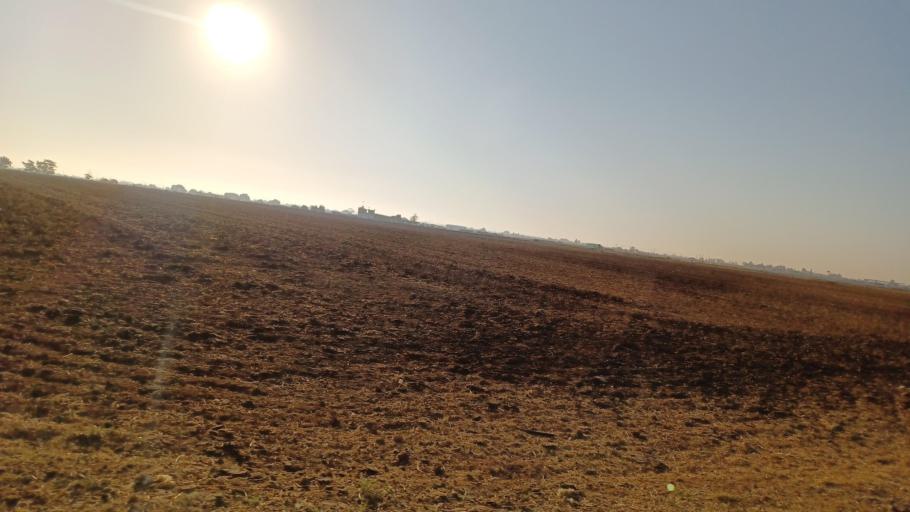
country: CY
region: Ammochostos
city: Achna
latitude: 35.0331
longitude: 33.7906
